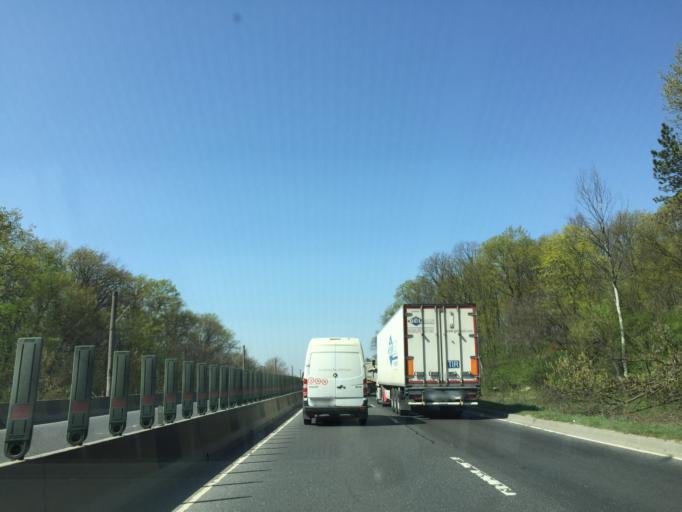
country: RO
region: Ilfov
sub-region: Comuna Otopeni
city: Otopeni
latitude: 44.5394
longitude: 26.1073
